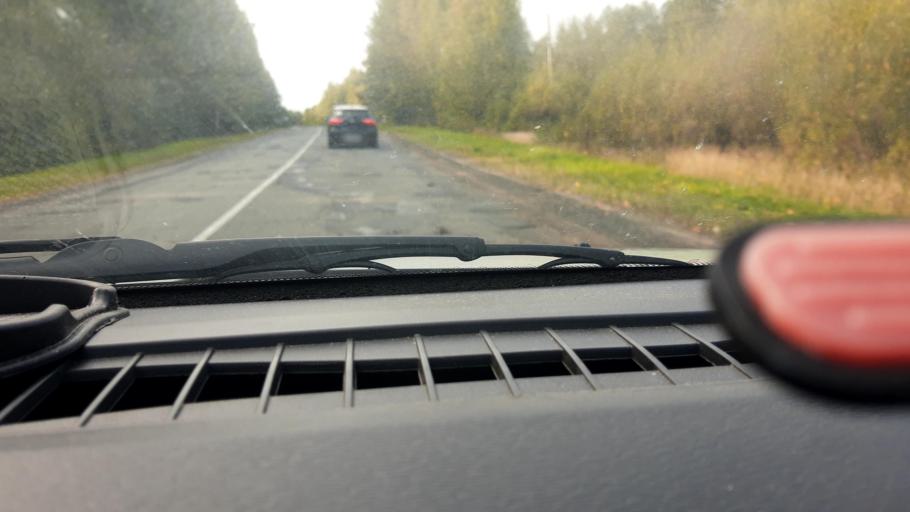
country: RU
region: Nizjnij Novgorod
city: Prudy
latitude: 57.3750
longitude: 46.1580
